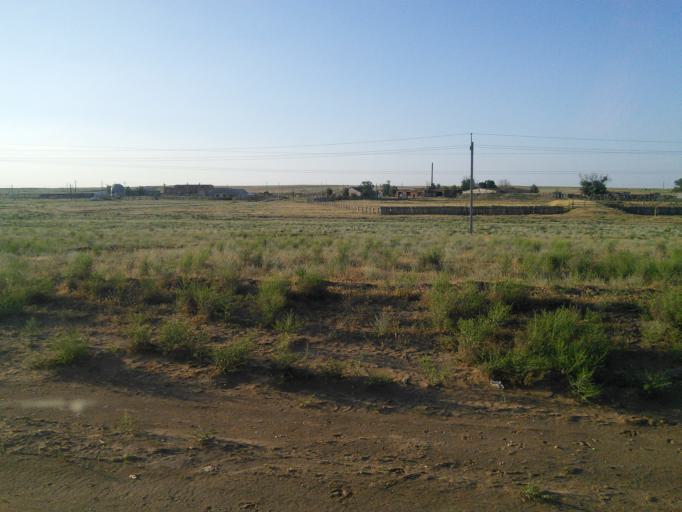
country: RU
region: Astrakhan
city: Ikryanoye
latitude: 46.2573
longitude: 47.4461
